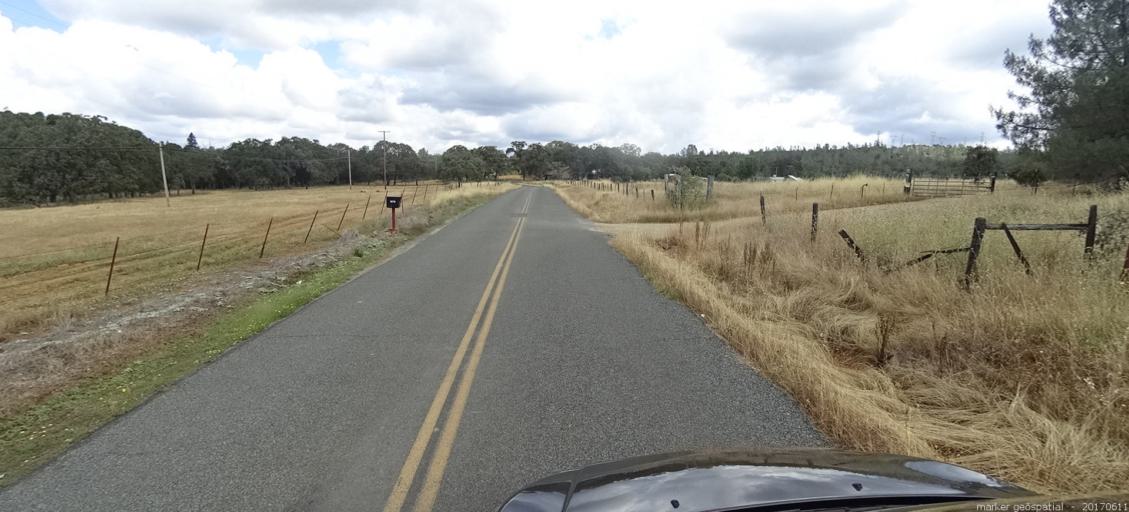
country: US
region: California
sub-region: Butte County
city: Oroville
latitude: 39.6139
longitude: -121.5263
